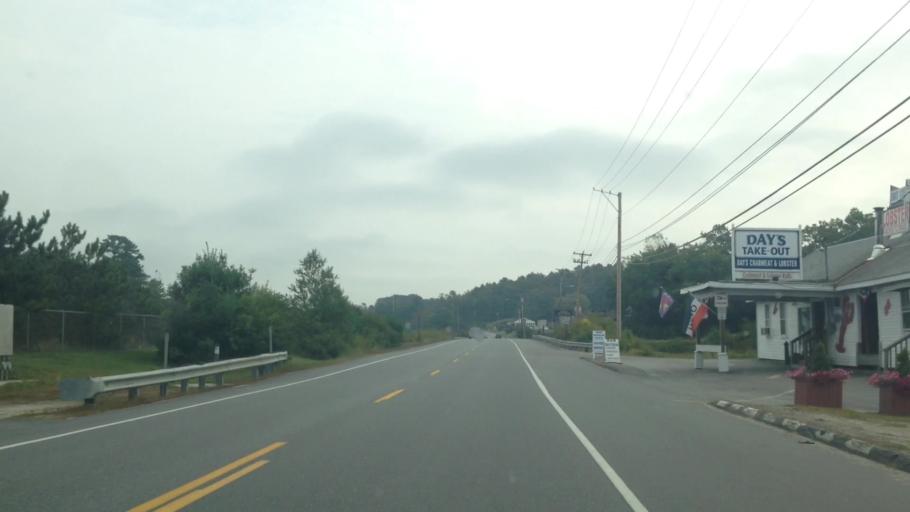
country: US
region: Maine
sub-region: Cumberland County
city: Yarmouth
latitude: 43.8115
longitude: -70.1565
